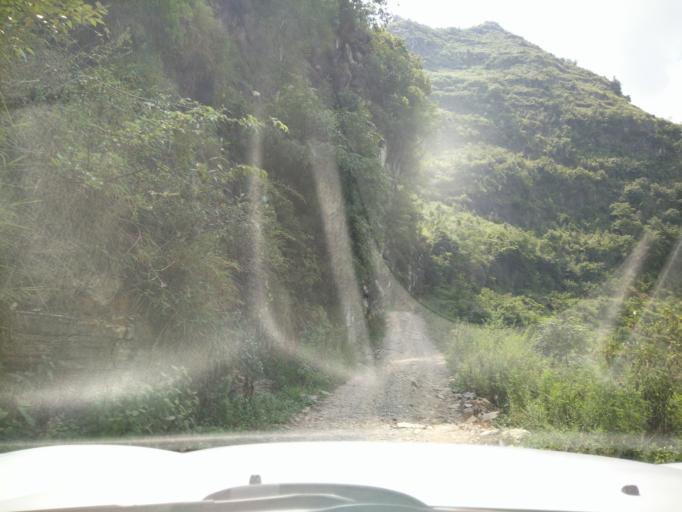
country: CN
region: Guangxi Zhuangzu Zizhiqu
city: Xinzhou
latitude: 25.0203
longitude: 105.7052
